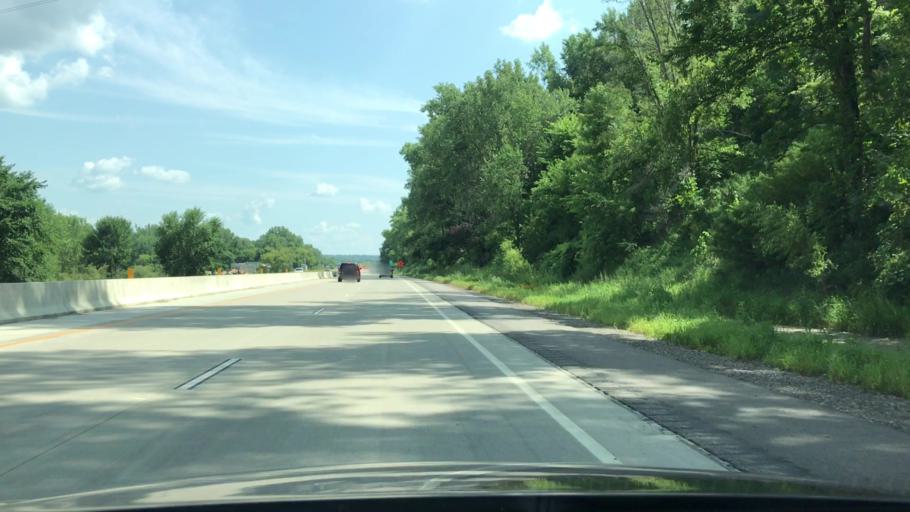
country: US
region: Minnesota
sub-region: Nicollet County
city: North Mankato
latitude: 44.2080
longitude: -94.0254
